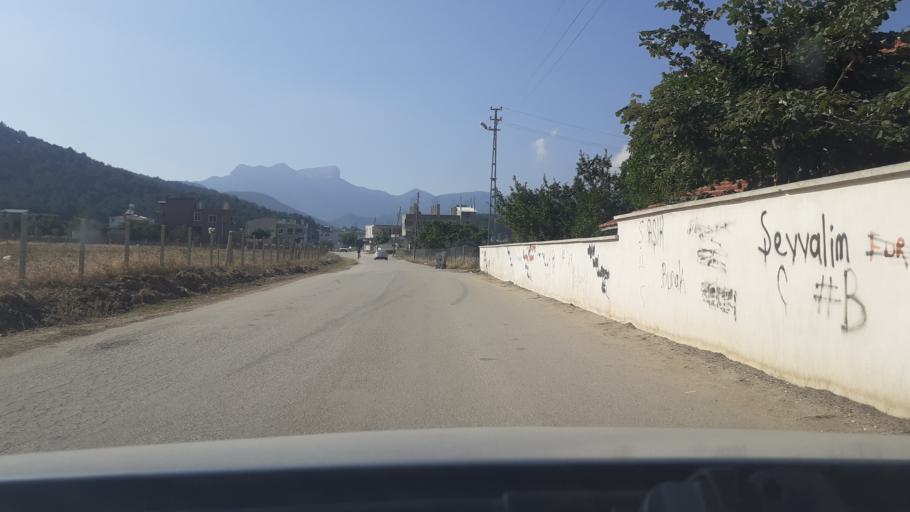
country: TR
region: Hatay
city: Gyuvench
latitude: 36.6217
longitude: 36.3436
